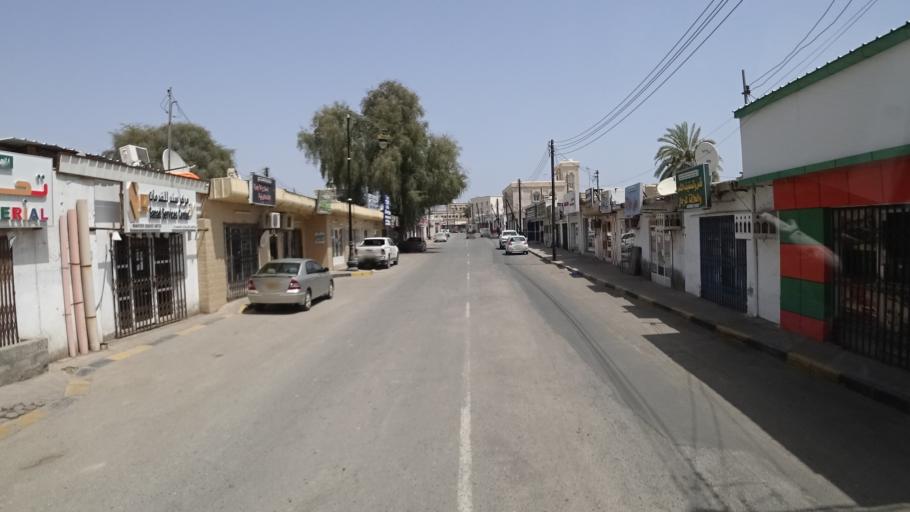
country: OM
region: Muhafazat Masqat
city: Muscat
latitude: 23.2608
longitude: 58.9155
